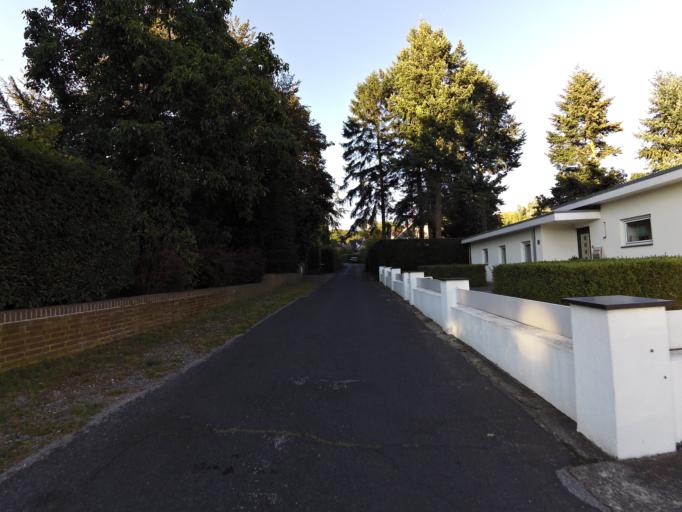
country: DE
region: North Rhine-Westphalia
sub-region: Regierungsbezirk Dusseldorf
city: Emmerich
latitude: 51.8661
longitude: 6.1734
